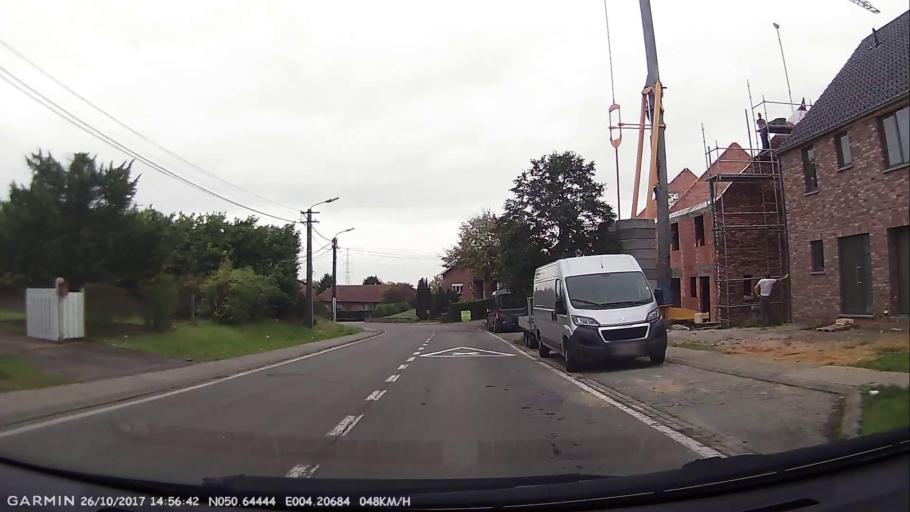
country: BE
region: Wallonia
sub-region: Province du Brabant Wallon
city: Tubize
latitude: 50.6445
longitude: 4.2069
